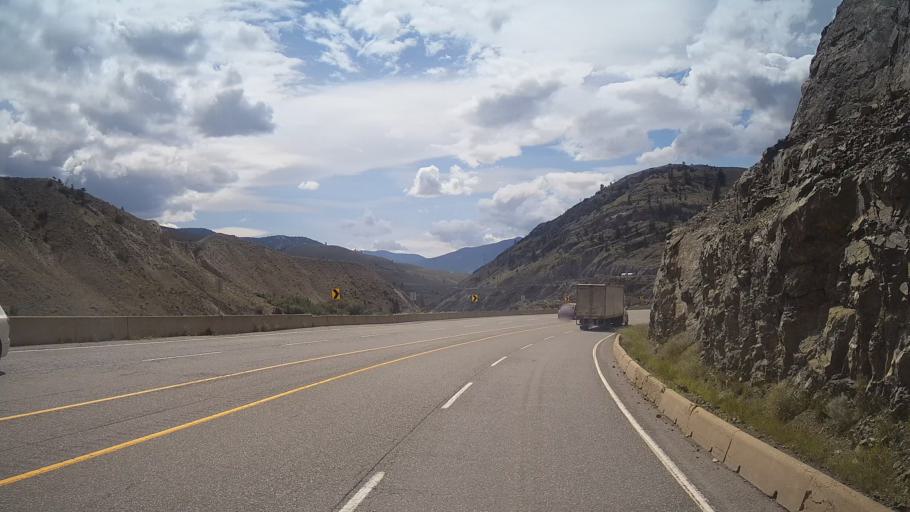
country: CA
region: British Columbia
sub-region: Thompson-Nicola Regional District
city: Ashcroft
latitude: 50.5123
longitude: -121.2831
